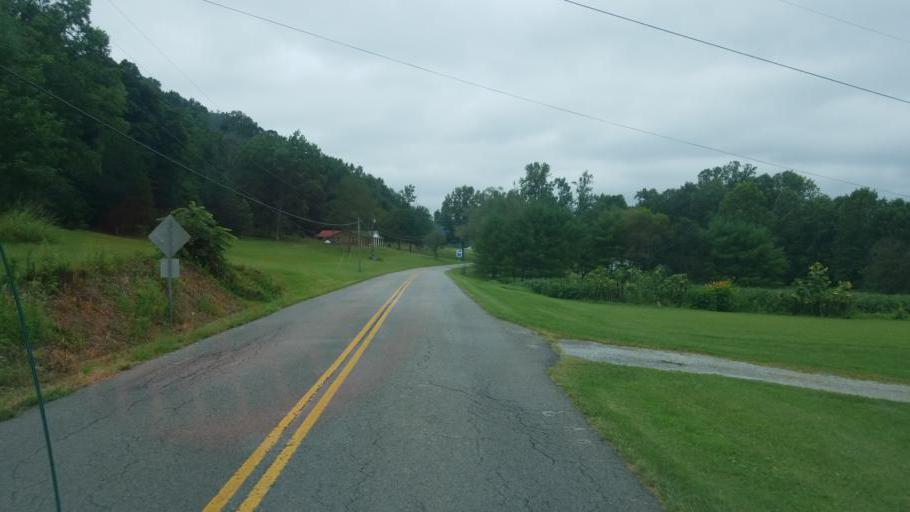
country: US
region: Kentucky
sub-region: Rowan County
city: Morehead
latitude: 38.3294
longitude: -83.5446
